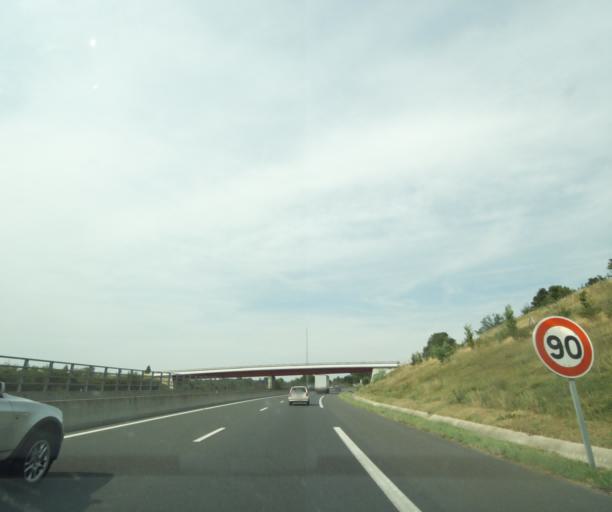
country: FR
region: Centre
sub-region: Departement d'Indre-et-Loire
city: La Membrolle-sur-Choisille
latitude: 47.4235
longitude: 0.6351
